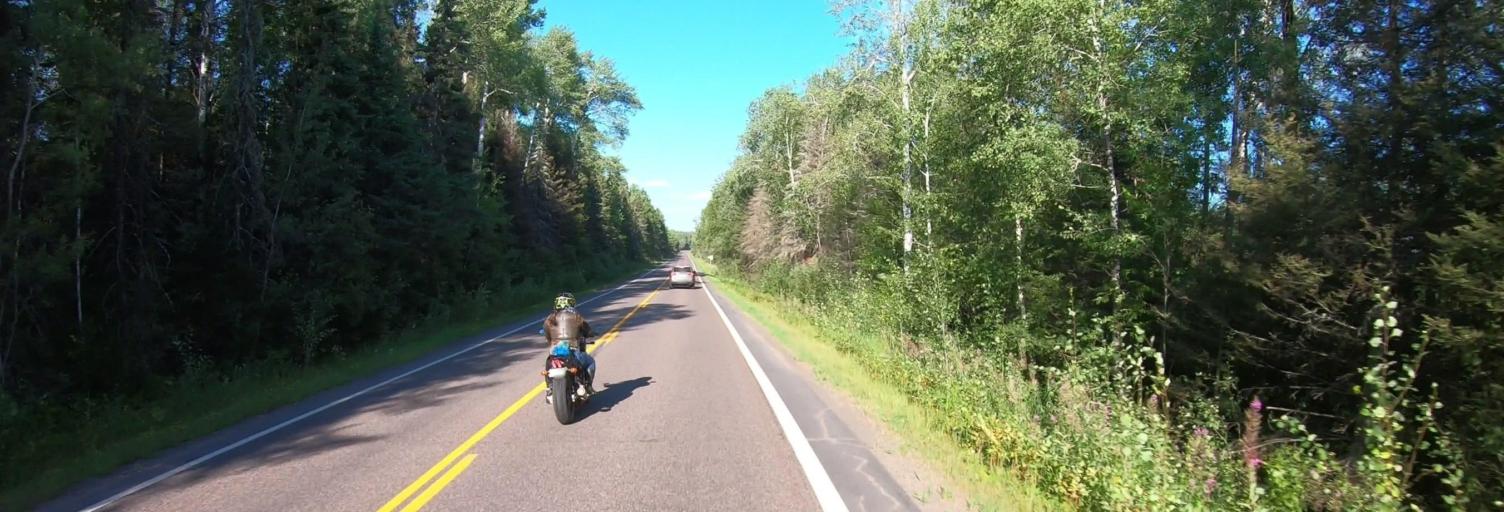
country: US
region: Minnesota
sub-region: Saint Louis County
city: Ely
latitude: 47.9316
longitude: -91.7081
